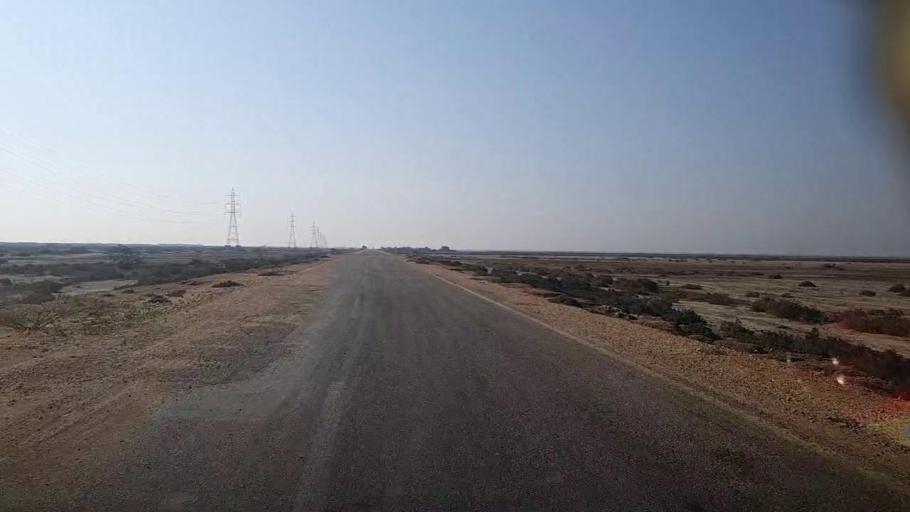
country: PK
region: Sindh
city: Gharo
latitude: 24.6213
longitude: 67.4969
